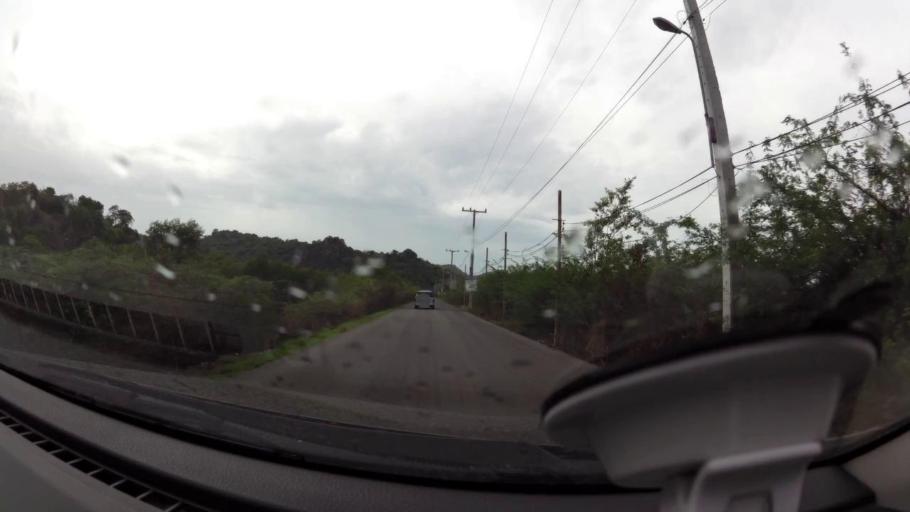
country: TH
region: Prachuap Khiri Khan
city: Pran Buri
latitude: 12.4210
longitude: 99.9800
